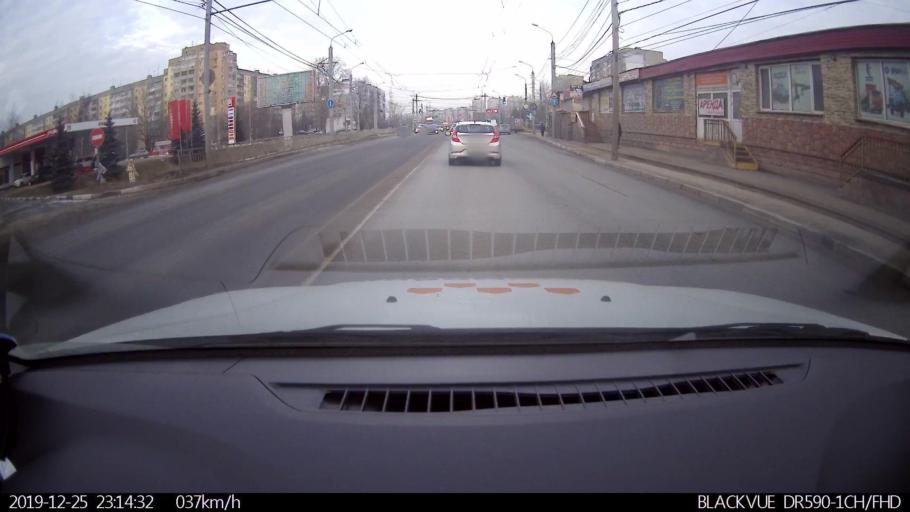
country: RU
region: Nizjnij Novgorod
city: Nizhniy Novgorod
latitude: 56.3340
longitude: 43.9194
